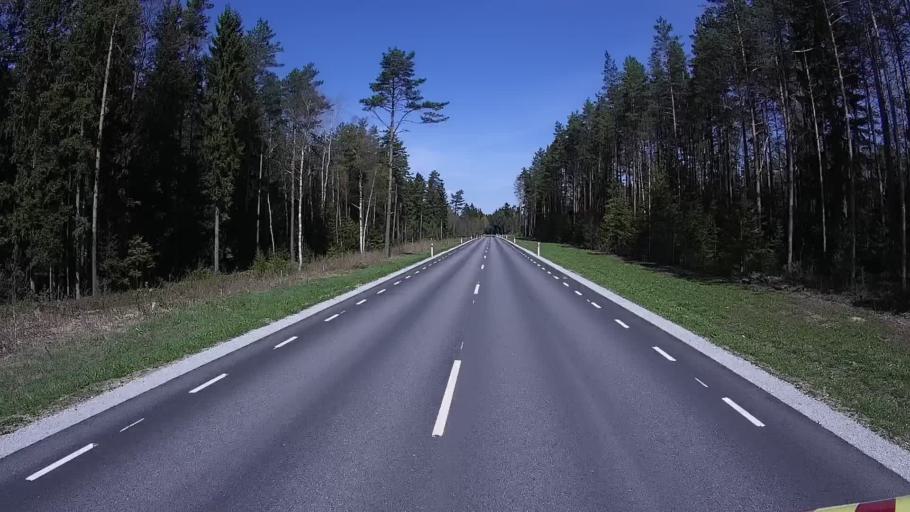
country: EE
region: Harju
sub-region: Nissi vald
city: Turba
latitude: 59.1426
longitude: 24.0764
